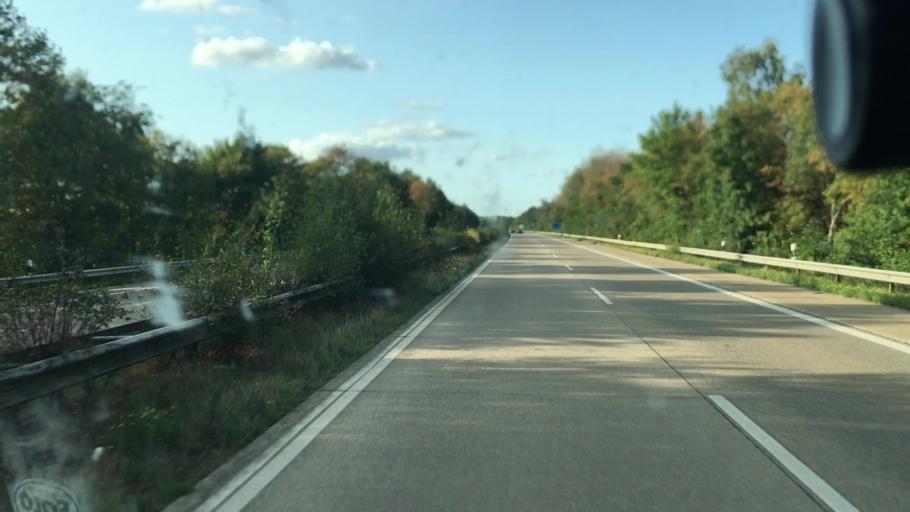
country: DE
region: Lower Saxony
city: Oldenburg
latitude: 53.1711
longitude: 8.2689
